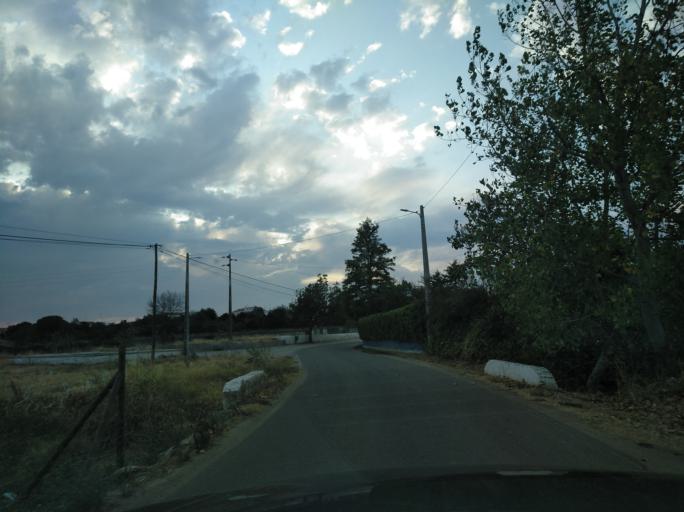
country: PT
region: Portalegre
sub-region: Campo Maior
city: Campo Maior
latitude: 39.0181
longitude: -7.0561
